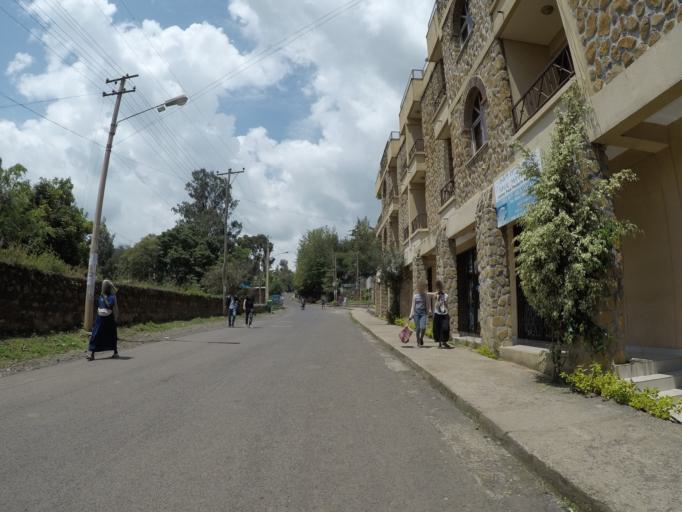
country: ET
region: Amhara
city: Gondar
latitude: 12.6113
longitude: 37.4708
